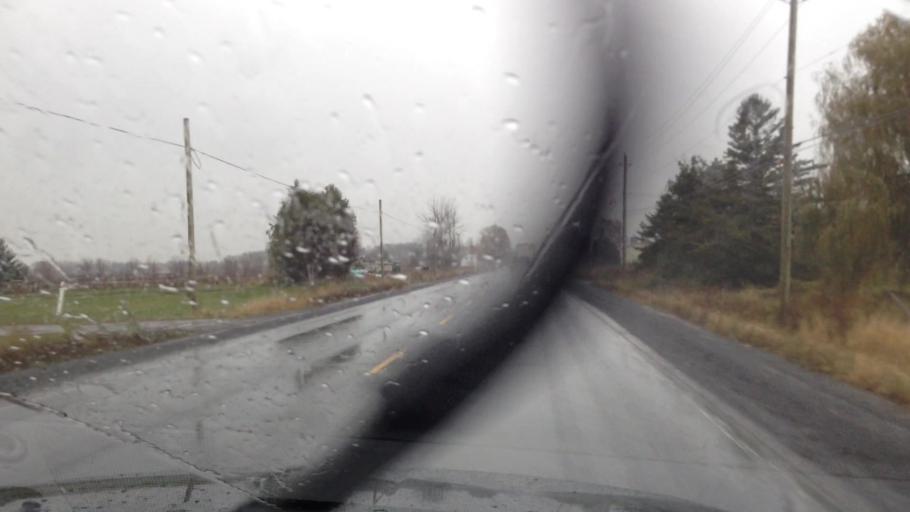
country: CA
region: Ontario
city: Bourget
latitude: 45.2843
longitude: -75.3191
